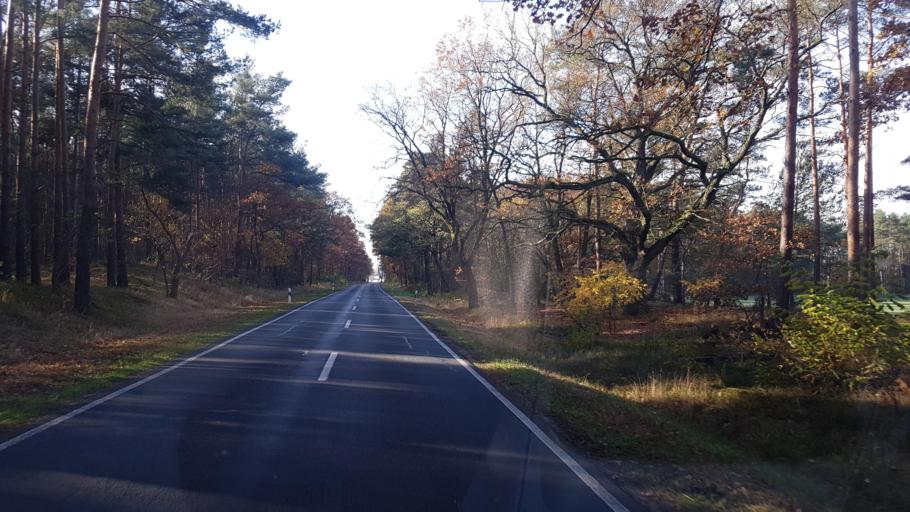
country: DE
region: Brandenburg
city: Golzow
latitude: 52.2812
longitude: 12.6154
